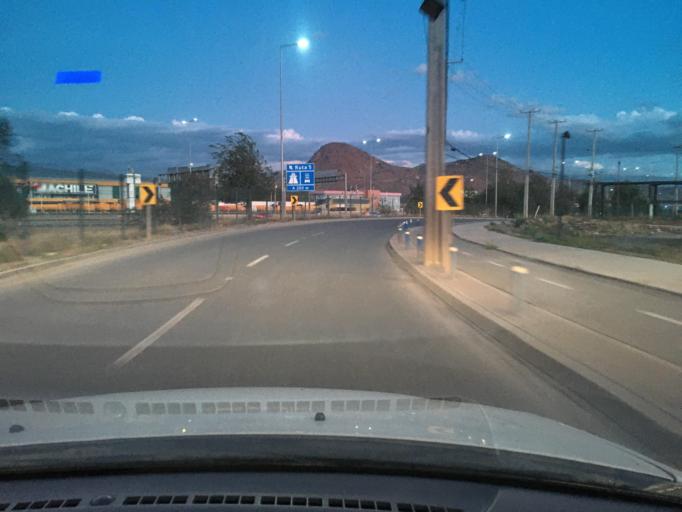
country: CL
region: Santiago Metropolitan
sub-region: Provincia de Chacabuco
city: Chicureo Abajo
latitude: -33.3025
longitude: -70.7295
